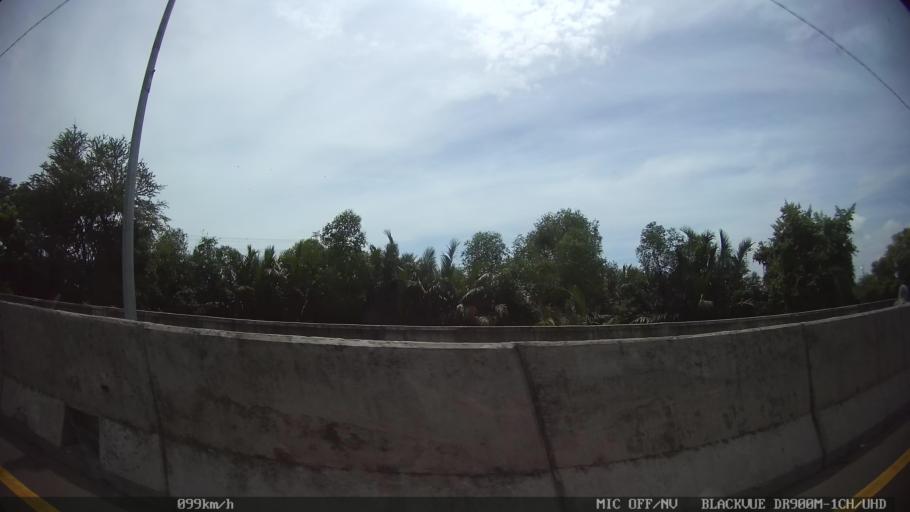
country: ID
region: North Sumatra
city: Labuhan Deli
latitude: 3.7447
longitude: 98.6797
